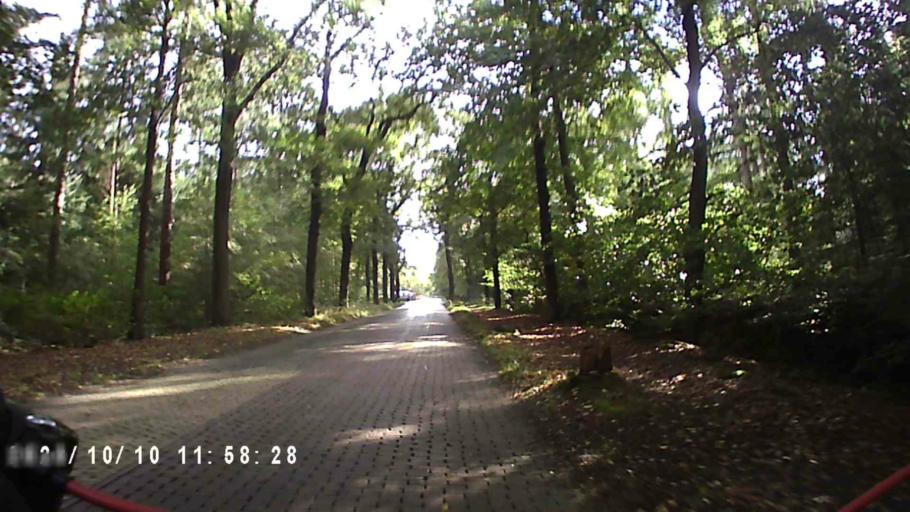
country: NL
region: Friesland
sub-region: Gemeente Smallingerland
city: Drachten
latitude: 53.0588
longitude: 6.0948
